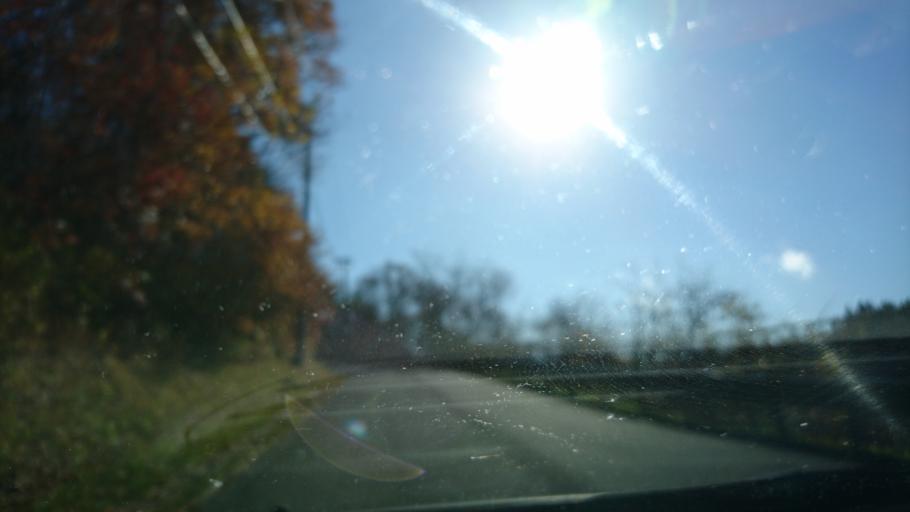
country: JP
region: Iwate
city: Ichinoseki
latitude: 38.9977
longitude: 141.0913
